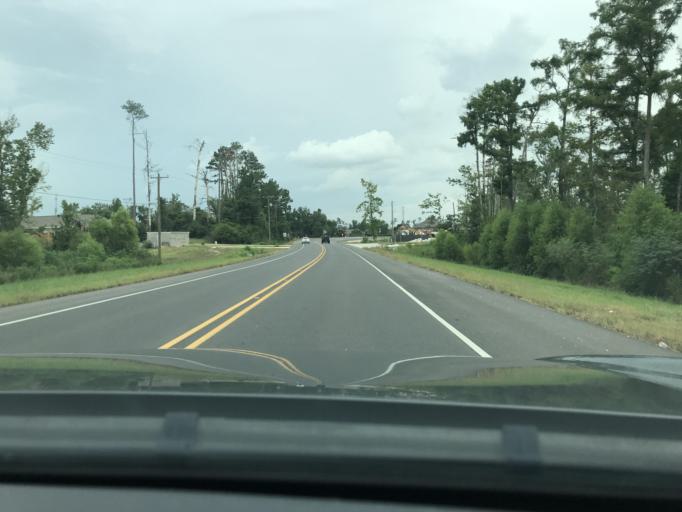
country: US
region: Louisiana
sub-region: Calcasieu Parish
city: Moss Bluff
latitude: 30.3022
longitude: -93.2463
